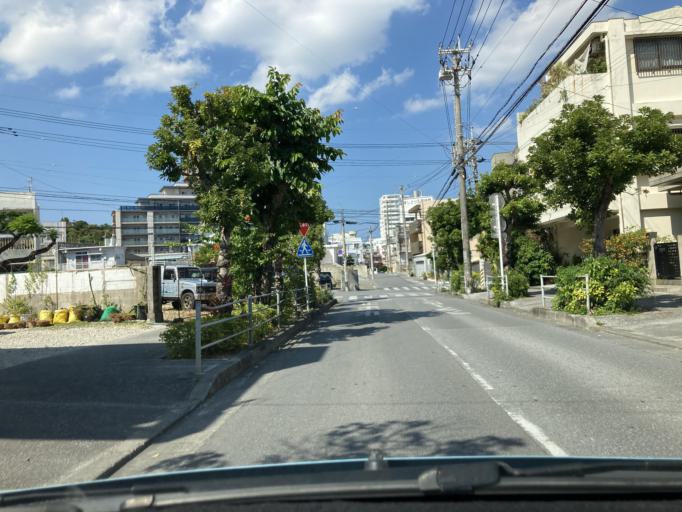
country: JP
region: Okinawa
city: Naha-shi
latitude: 26.2025
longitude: 127.6899
